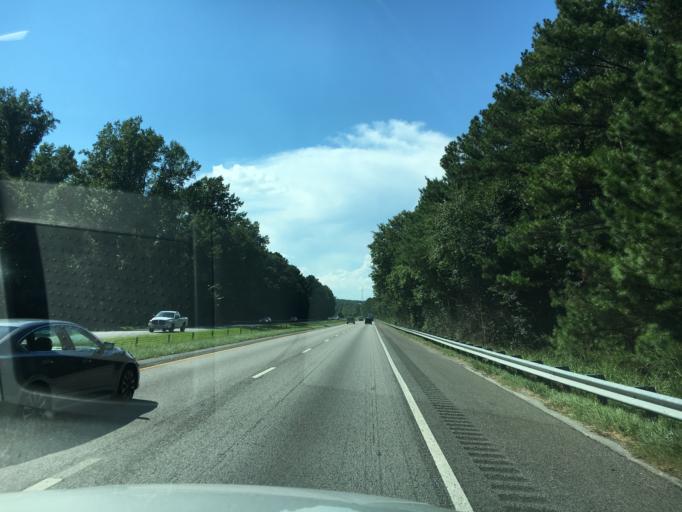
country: US
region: South Carolina
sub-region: Greenville County
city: Fountain Inn
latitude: 34.6196
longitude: -82.0875
